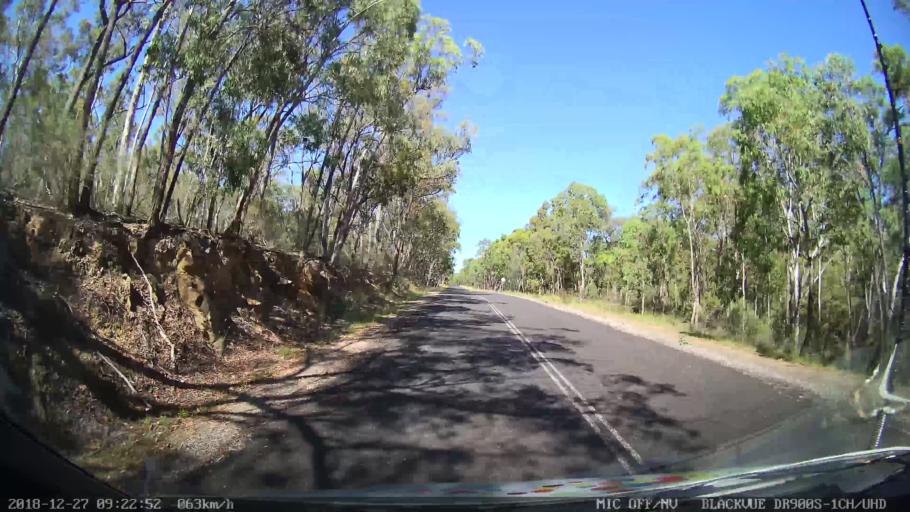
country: AU
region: New South Wales
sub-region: Lithgow
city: Portland
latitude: -33.1236
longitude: 150.0034
